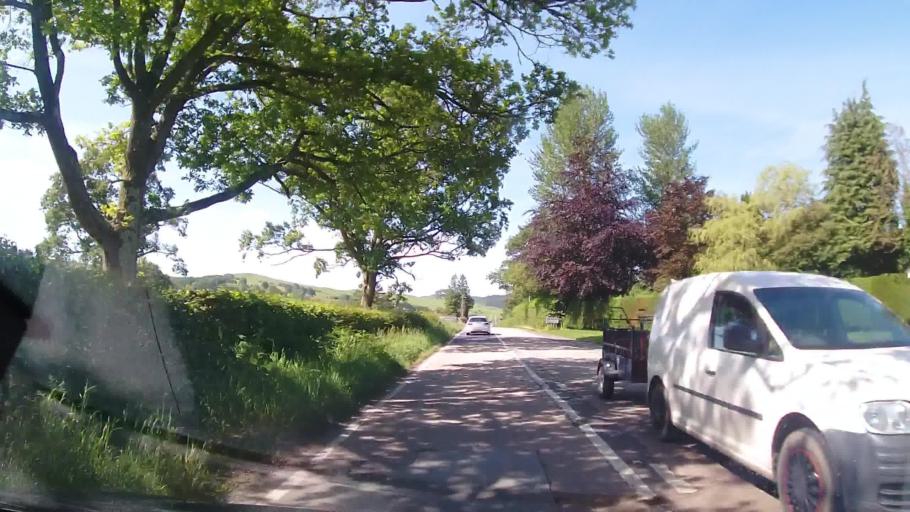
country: GB
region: Wales
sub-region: Sir Powys
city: Machynlleth
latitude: 52.5956
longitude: -3.8030
